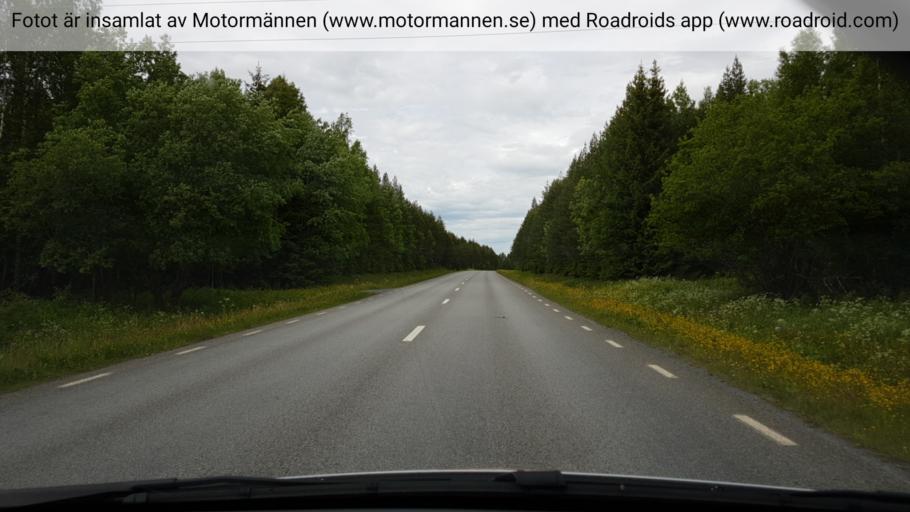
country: SE
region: Jaemtland
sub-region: Krokoms Kommun
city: Valla
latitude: 63.2710
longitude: 13.9529
